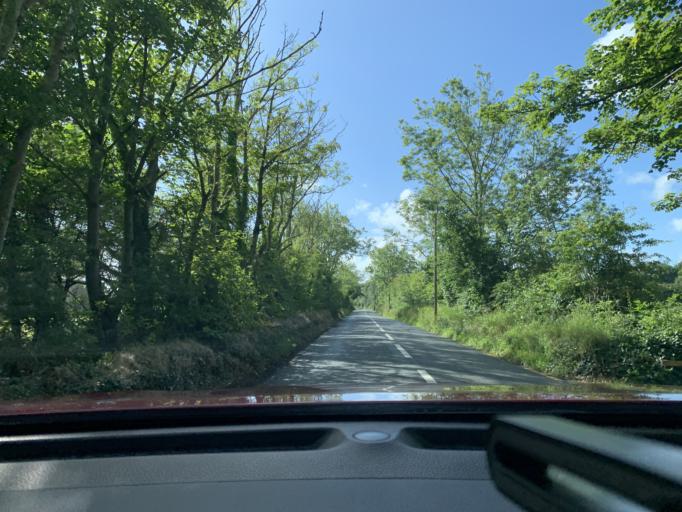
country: IE
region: Connaught
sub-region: Sligo
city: Strandhill
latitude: 54.3489
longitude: -8.5608
